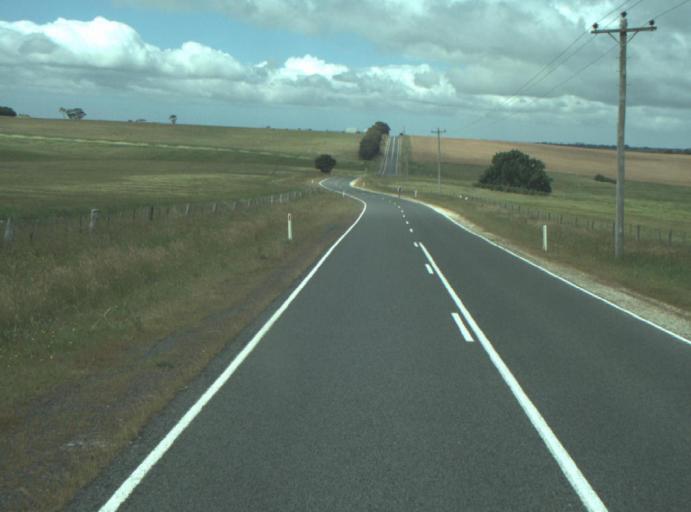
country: AU
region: Victoria
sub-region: Greater Geelong
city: Wandana Heights
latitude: -38.1759
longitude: 144.2712
